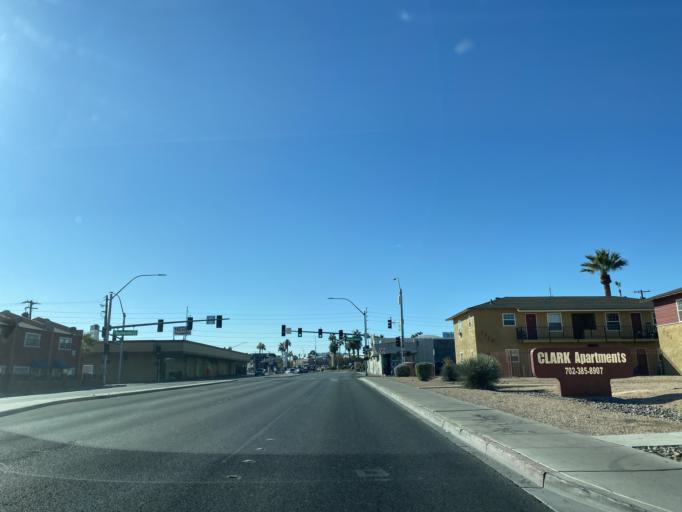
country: US
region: Nevada
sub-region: Clark County
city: Las Vegas
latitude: 36.1606
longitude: -115.1360
